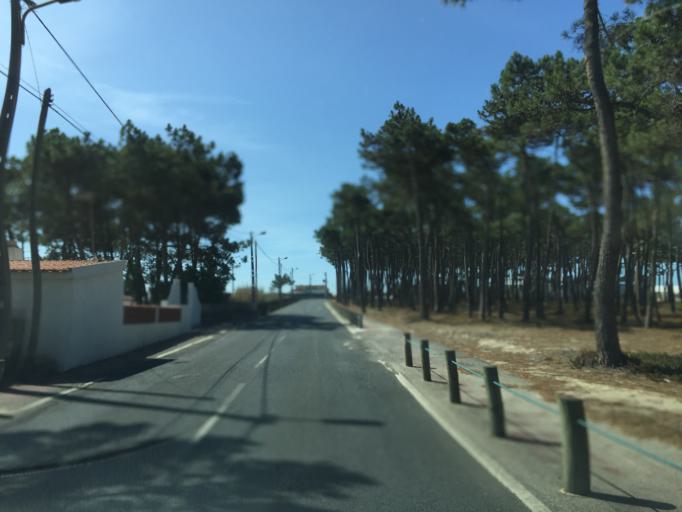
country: PT
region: Lisbon
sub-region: Torres Vedras
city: Silveira
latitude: 39.1556
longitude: -9.3611
